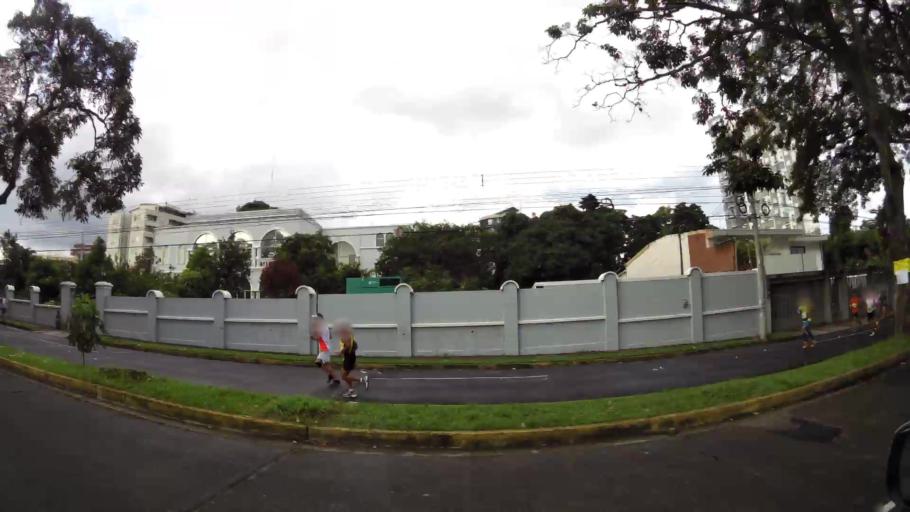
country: CR
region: San Jose
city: Colima
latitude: 9.9400
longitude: -84.1106
